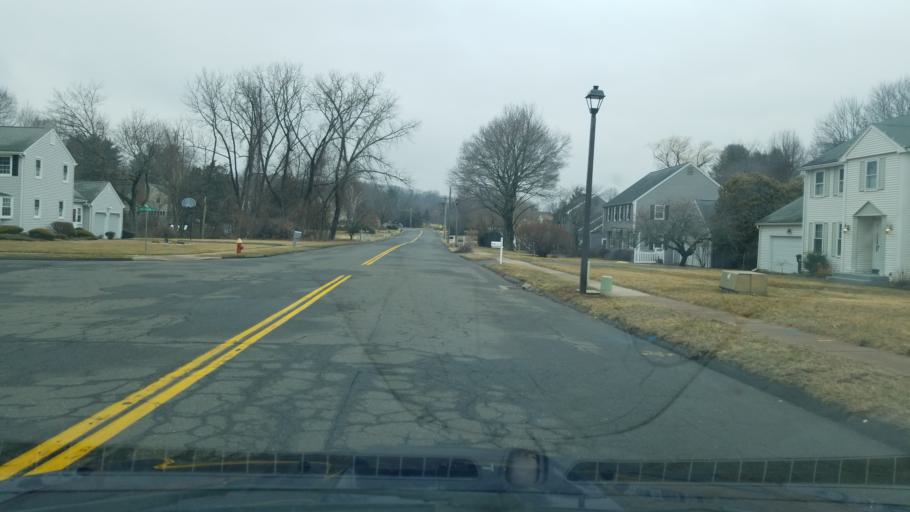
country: US
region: Connecticut
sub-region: Hartford County
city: Newington
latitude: 41.6730
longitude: -72.6827
